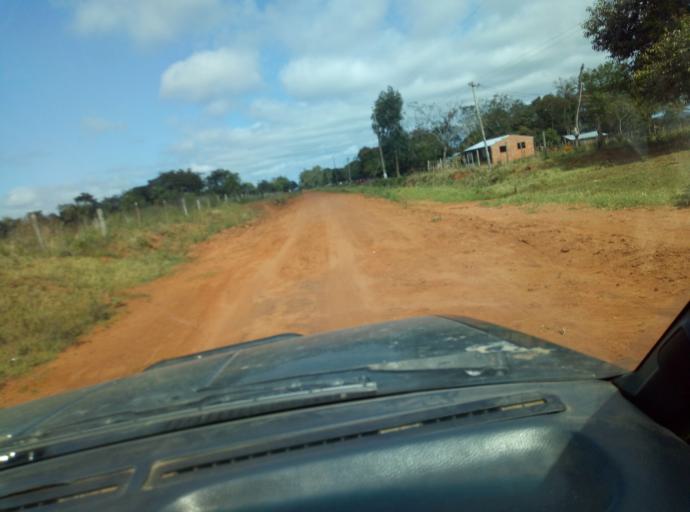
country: PY
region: Caaguazu
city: Doctor Cecilio Baez
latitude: -25.1516
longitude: -56.2910
